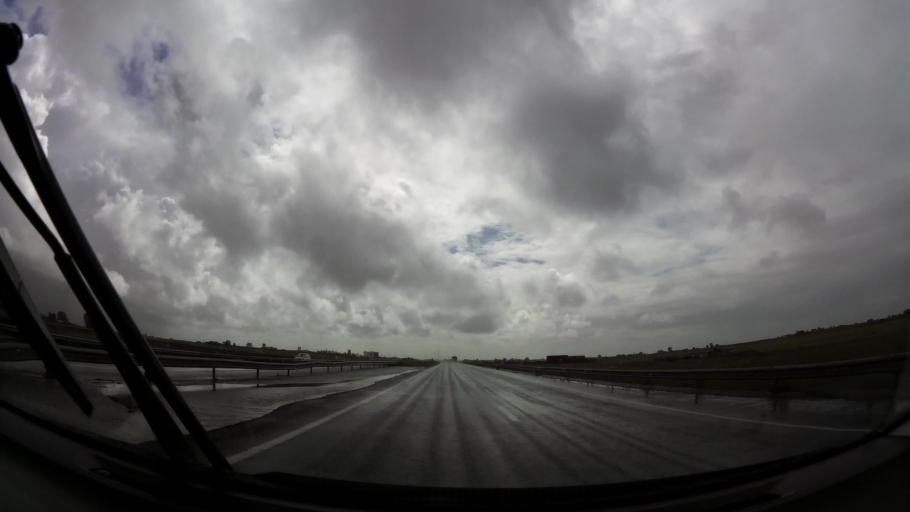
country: MA
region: Grand Casablanca
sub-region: Nouaceur
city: Dar Bouazza
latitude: 33.3921
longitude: -7.8647
